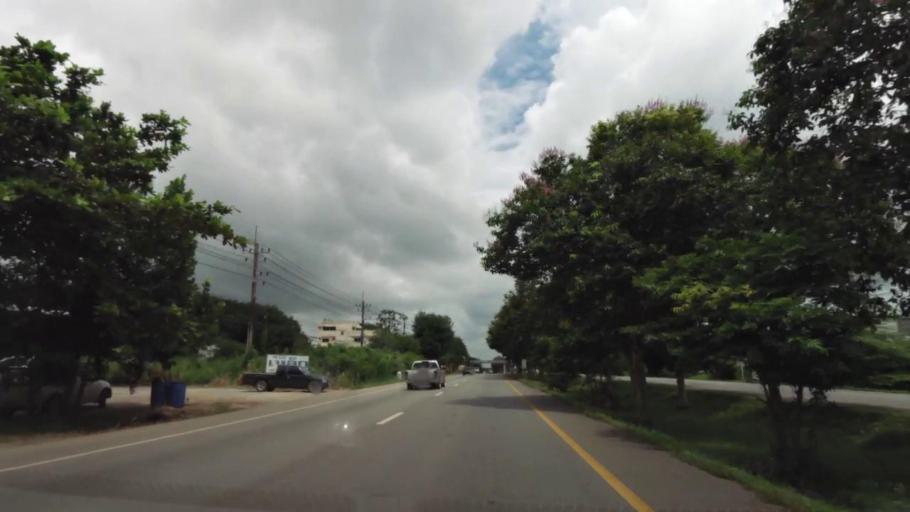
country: TH
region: Chanthaburi
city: Na Yai Am
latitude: 12.7692
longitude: 101.8467
